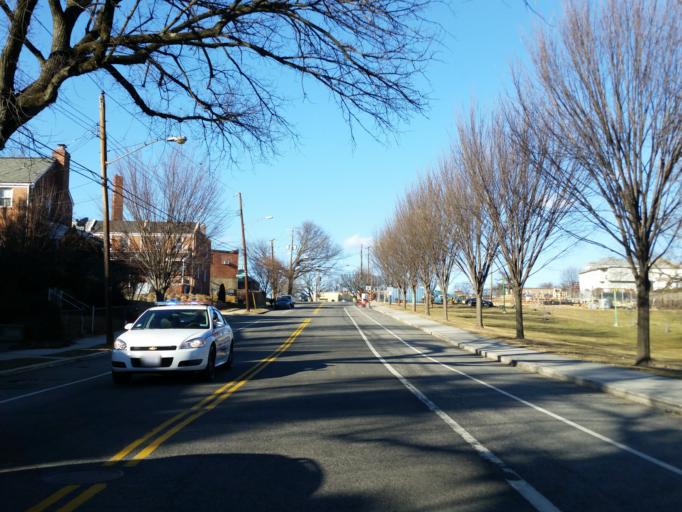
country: US
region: Maryland
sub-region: Prince George's County
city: Mount Rainier
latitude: 38.9261
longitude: -76.9789
